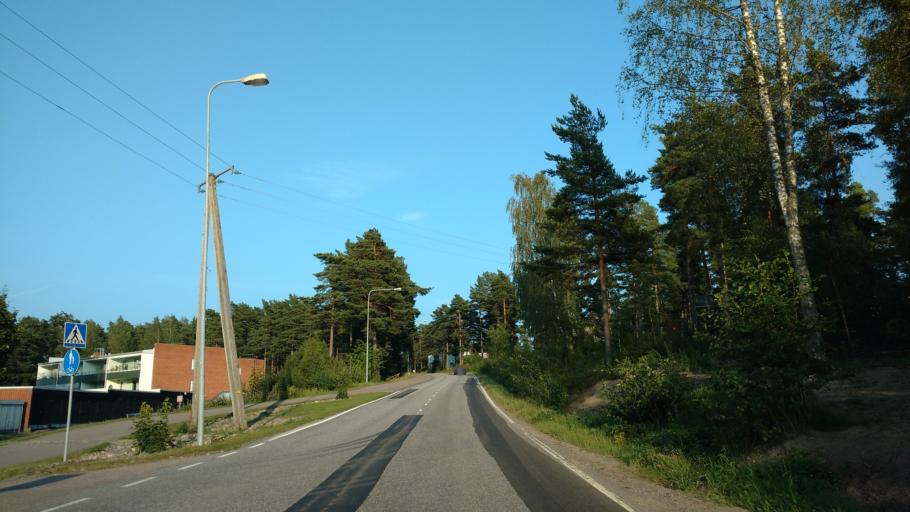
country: FI
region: Varsinais-Suomi
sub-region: Aboland-Turunmaa
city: Dragsfjaerd
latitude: 60.0728
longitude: 22.4652
